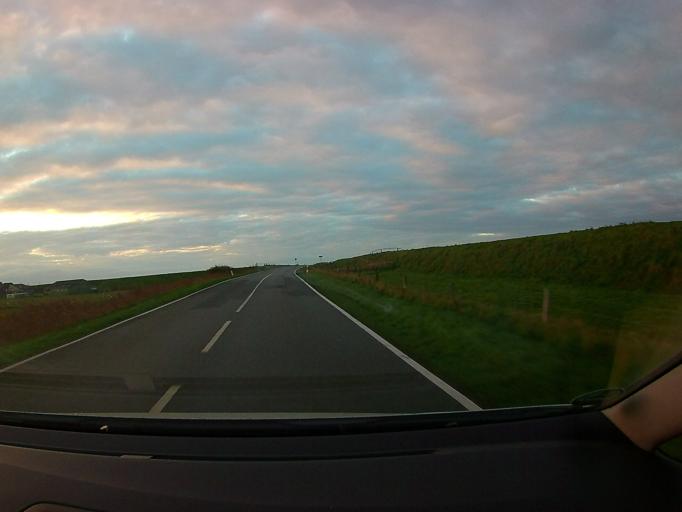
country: DE
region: Schleswig-Holstein
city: Galmsbull
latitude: 54.7055
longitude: 8.7549
